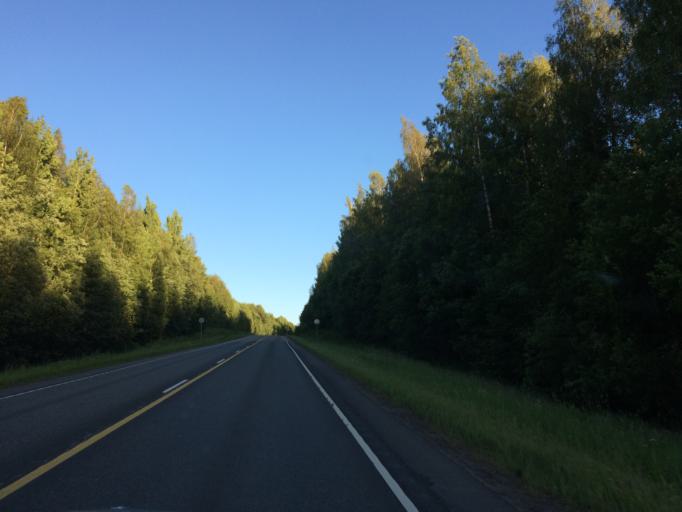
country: FI
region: Haeme
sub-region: Riihimaeki
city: Riihimaeki
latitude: 60.7655
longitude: 24.7107
